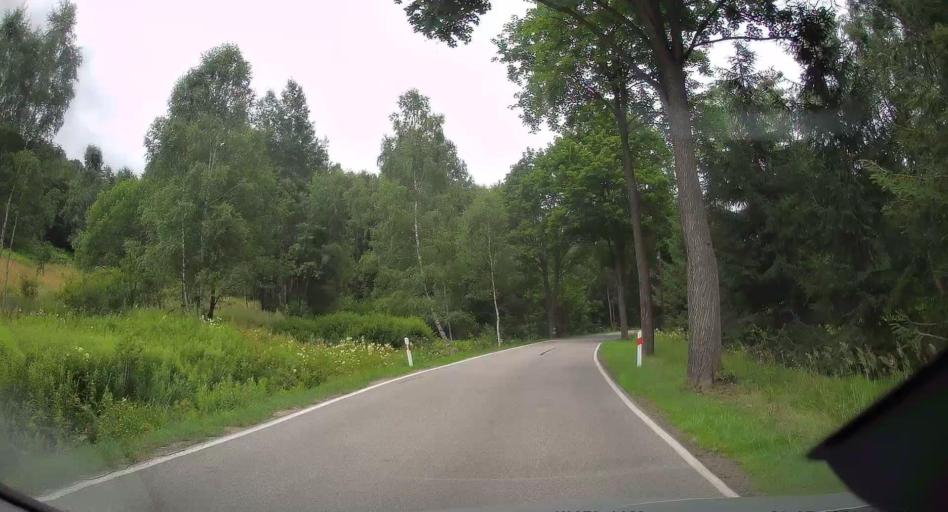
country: PL
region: Lower Silesian Voivodeship
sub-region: Powiat walbrzyski
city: Jedlina-Zdroj
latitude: 50.7288
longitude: 16.3714
